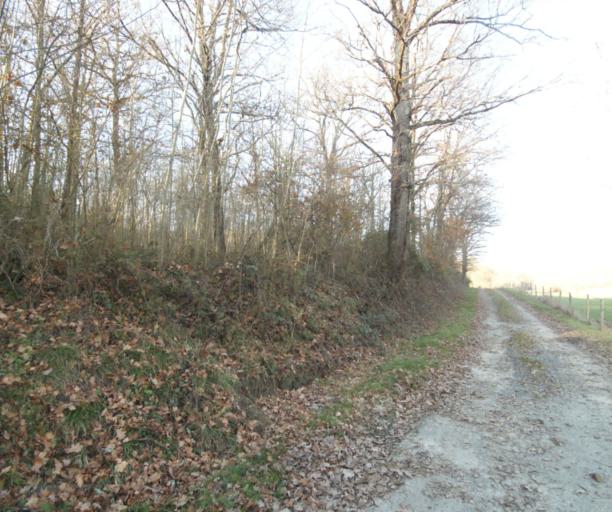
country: FR
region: Midi-Pyrenees
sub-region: Departement du Tarn-et-Garonne
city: Moissac
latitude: 44.1398
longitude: 1.1303
